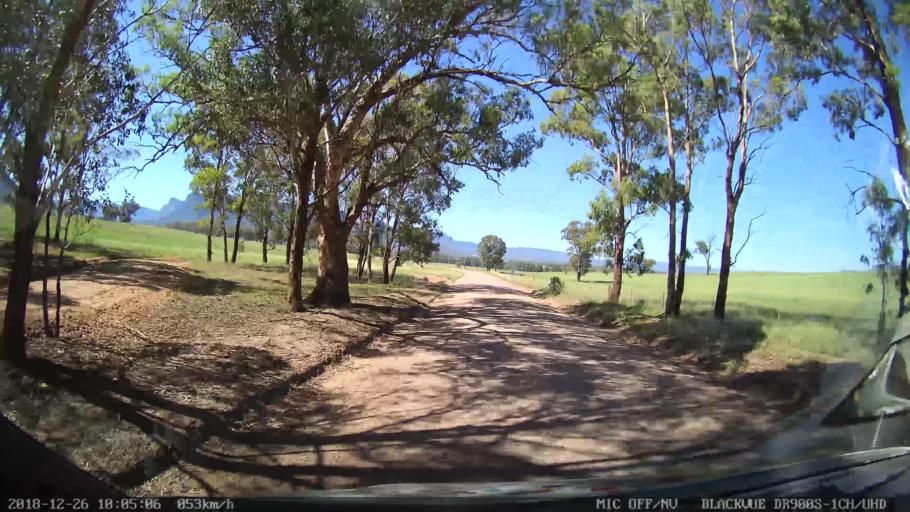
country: AU
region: New South Wales
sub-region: Mid-Western Regional
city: Kandos
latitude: -33.0756
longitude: 150.2122
